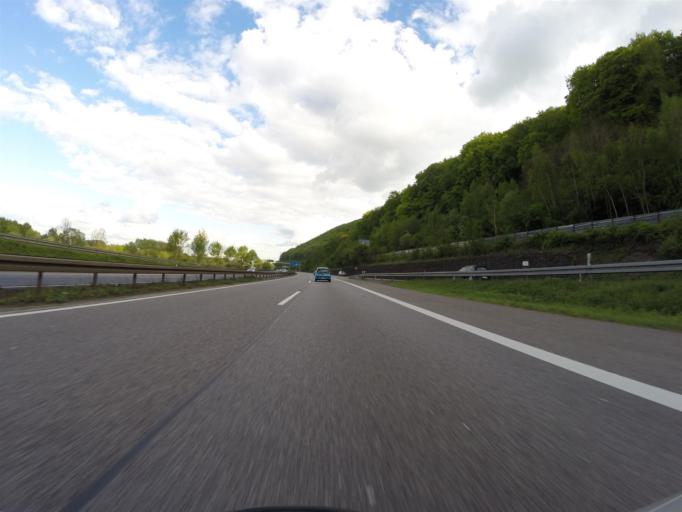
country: DE
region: Saarland
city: Wallerfangen
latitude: 49.3437
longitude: 6.7041
